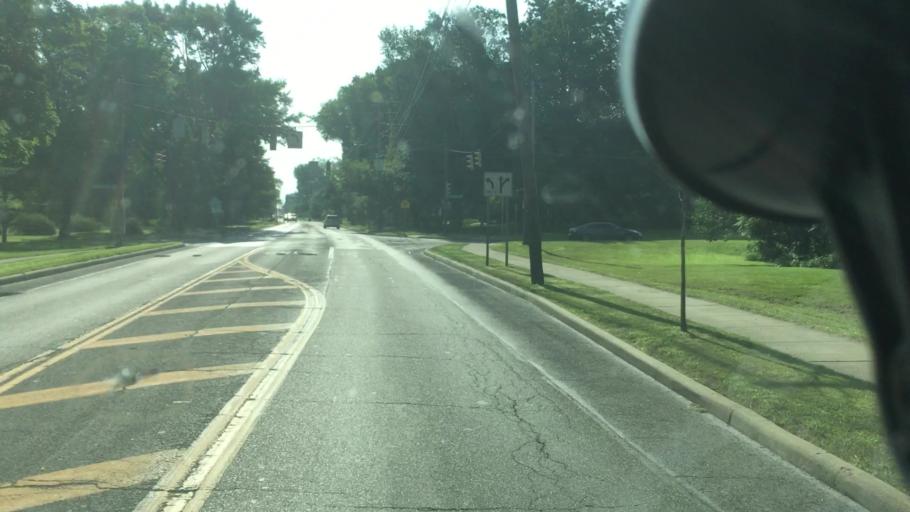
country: US
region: Ohio
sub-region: Mahoning County
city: Poland
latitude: 41.0237
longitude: -80.6078
